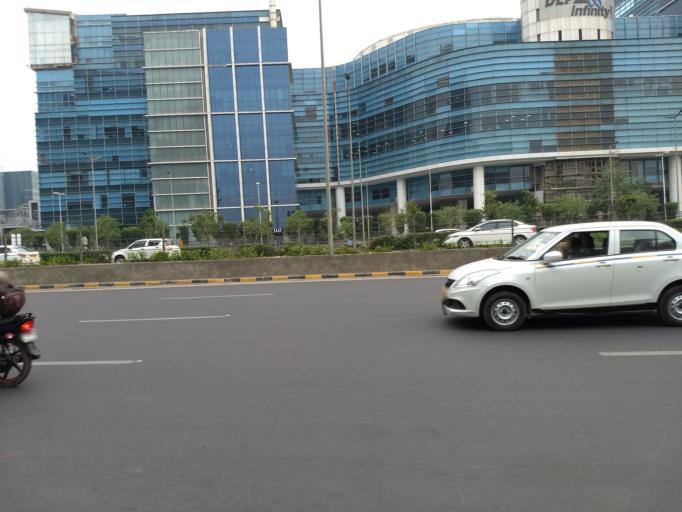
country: IN
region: Haryana
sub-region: Gurgaon
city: Gurgaon
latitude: 28.4966
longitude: 77.0921
